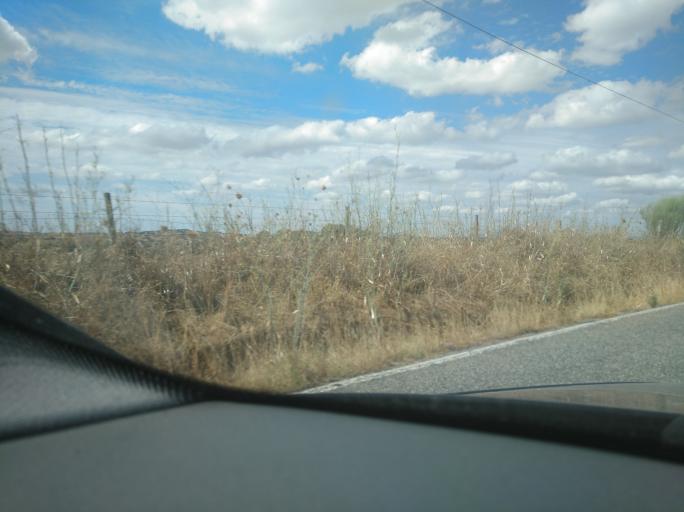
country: PT
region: Portalegre
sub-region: Arronches
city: Arronches
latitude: 39.0793
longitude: -7.3659
